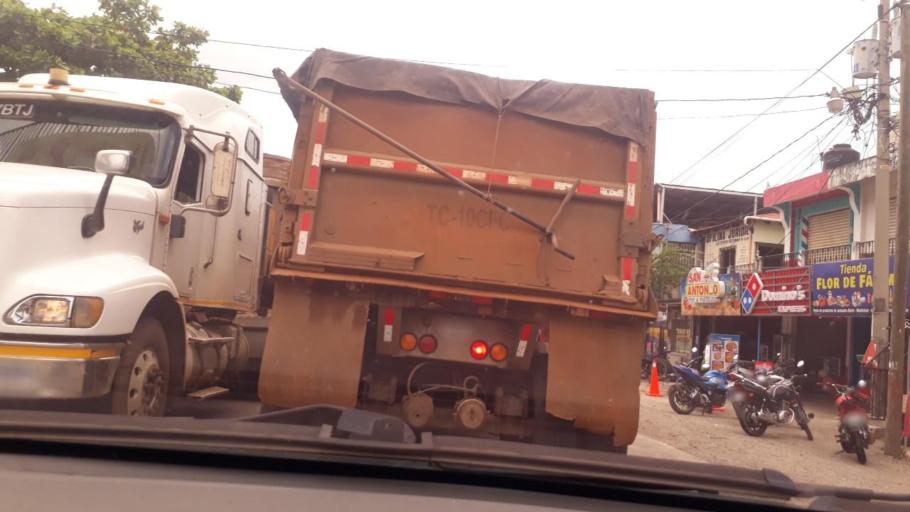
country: GT
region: Izabal
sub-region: Municipio de Los Amates
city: Los Amates
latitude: 15.2553
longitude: -89.0966
